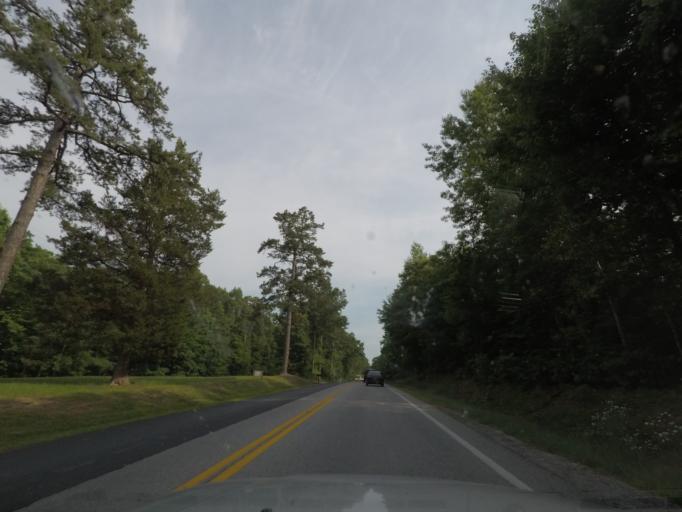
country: US
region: Virginia
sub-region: Prince Edward County
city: Hampden Sydney
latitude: 37.1667
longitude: -78.4405
